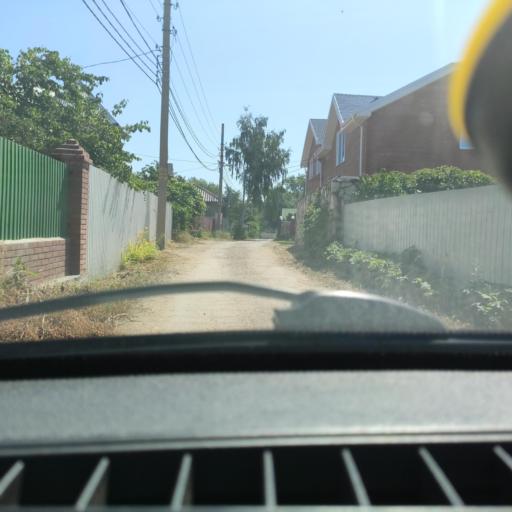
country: RU
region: Samara
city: Zhigulevsk
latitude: 53.4513
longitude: 49.5243
